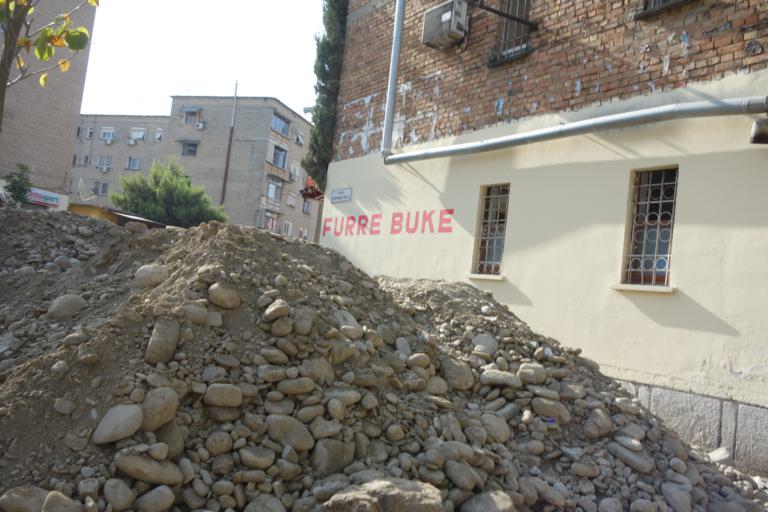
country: AL
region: Tirane
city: Tirana
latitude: 41.3386
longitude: 19.8404
